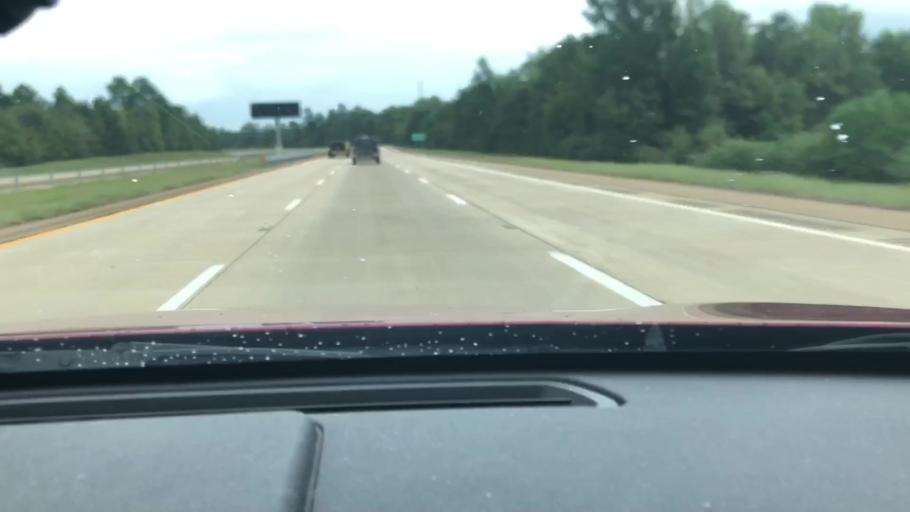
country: US
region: Texas
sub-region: Bowie County
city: Texarkana
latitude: 33.4009
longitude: -94.0075
